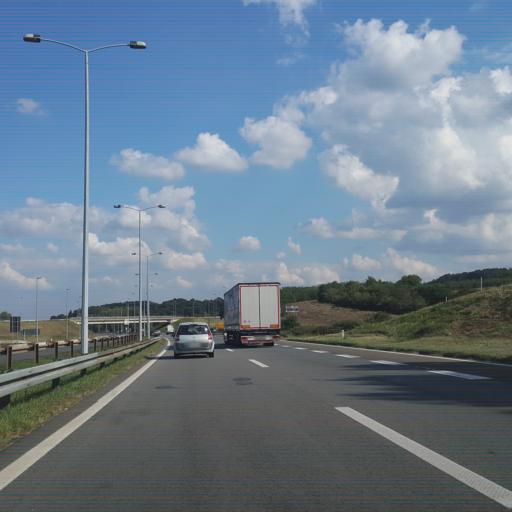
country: RS
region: Central Serbia
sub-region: Belgrade
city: Sopot
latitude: 44.5660
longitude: 20.6635
